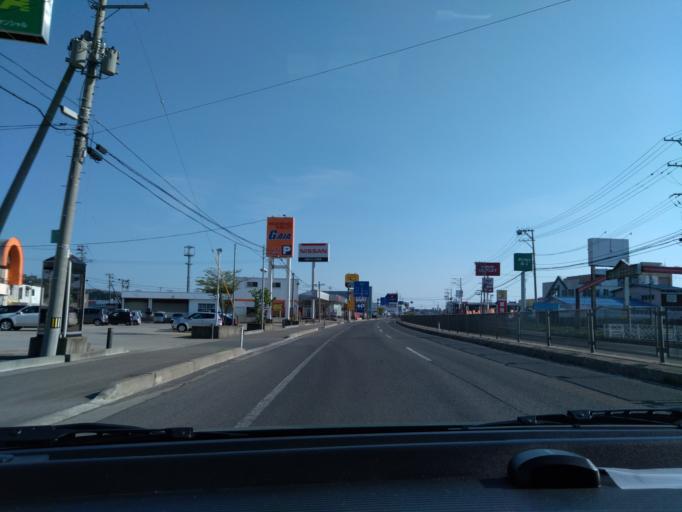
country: JP
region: Akita
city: Yokotemachi
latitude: 39.3050
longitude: 140.5577
